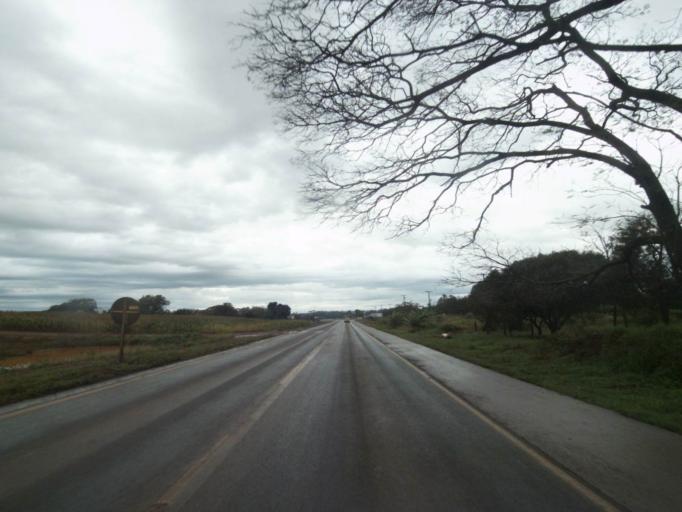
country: BR
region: Parana
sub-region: Toledo
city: Toledo
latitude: -24.6955
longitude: -53.7409
